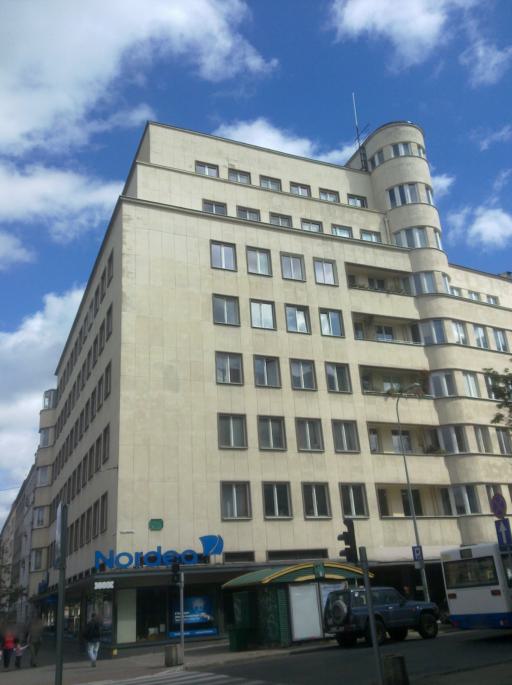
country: PL
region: Pomeranian Voivodeship
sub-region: Gdynia
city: Gdynia
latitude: 54.5196
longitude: 18.5354
